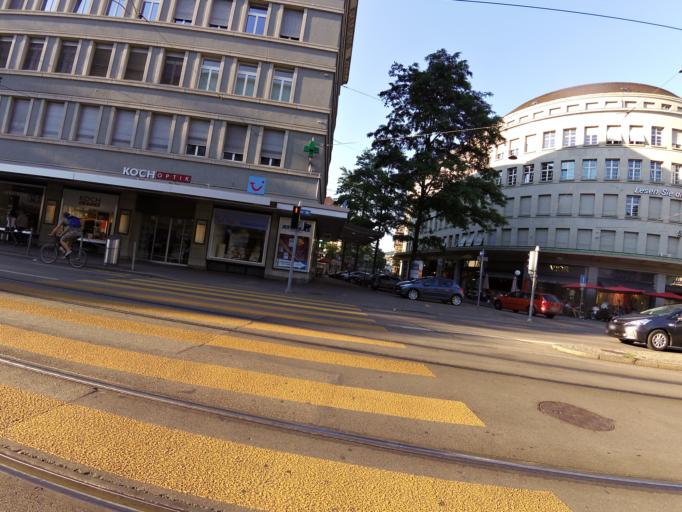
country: CH
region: Zurich
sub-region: Bezirk Zuerich
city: Zuerich (Kreis 1) / City
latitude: 47.3727
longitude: 8.5342
